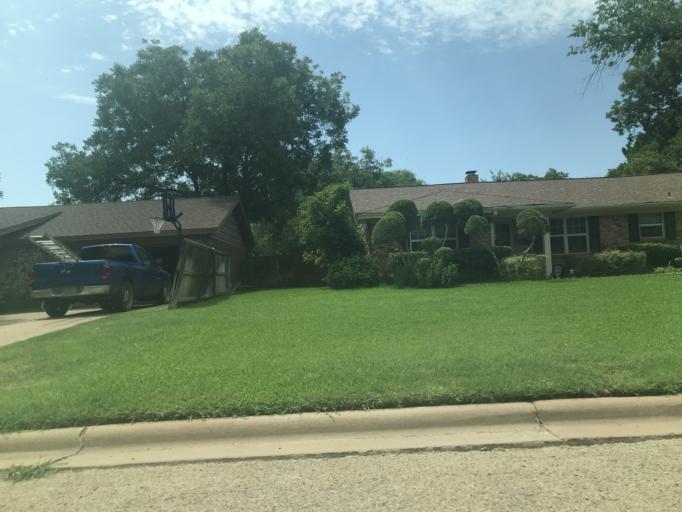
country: US
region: Texas
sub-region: Taylor County
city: Abilene
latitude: 32.4210
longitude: -99.7770
